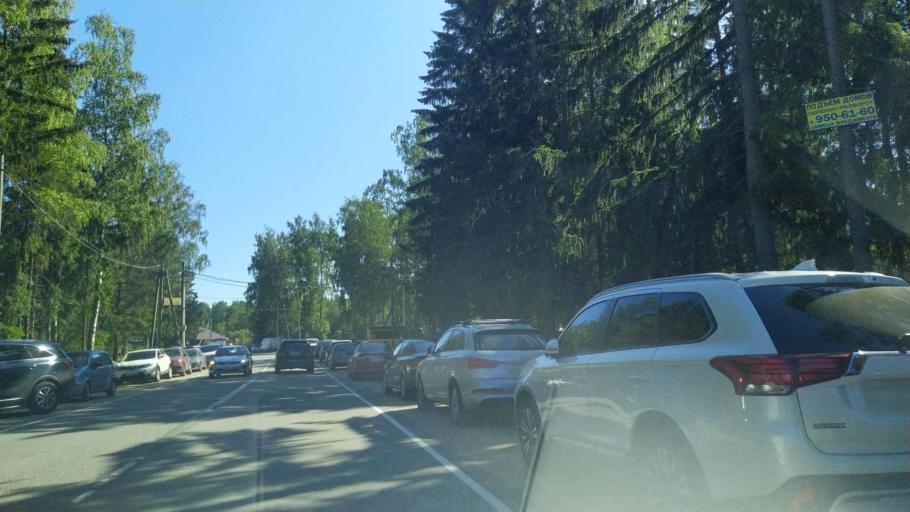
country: RU
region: Leningrad
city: Borisova Griva
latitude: 60.1217
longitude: 31.0742
